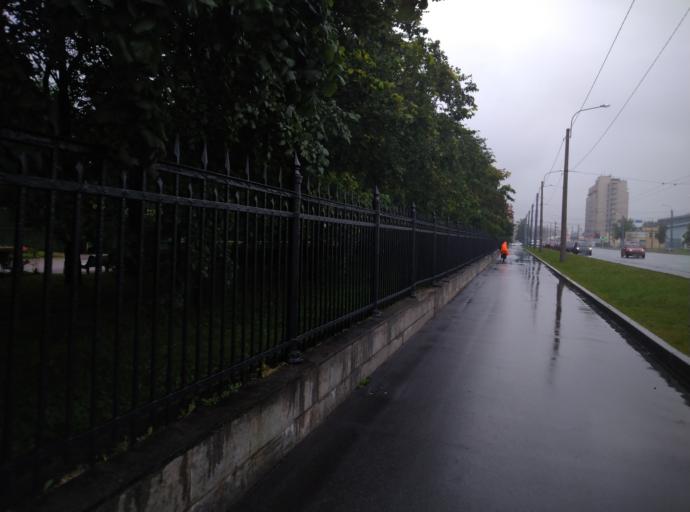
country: RU
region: St.-Petersburg
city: Kupchino
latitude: 59.8699
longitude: 30.3364
